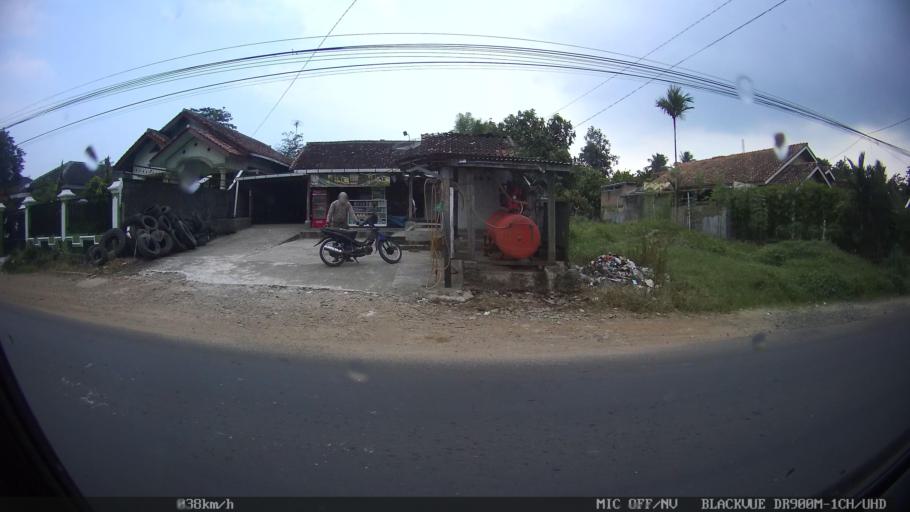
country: ID
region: Lampung
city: Gedongtataan
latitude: -5.3673
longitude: 105.1409
